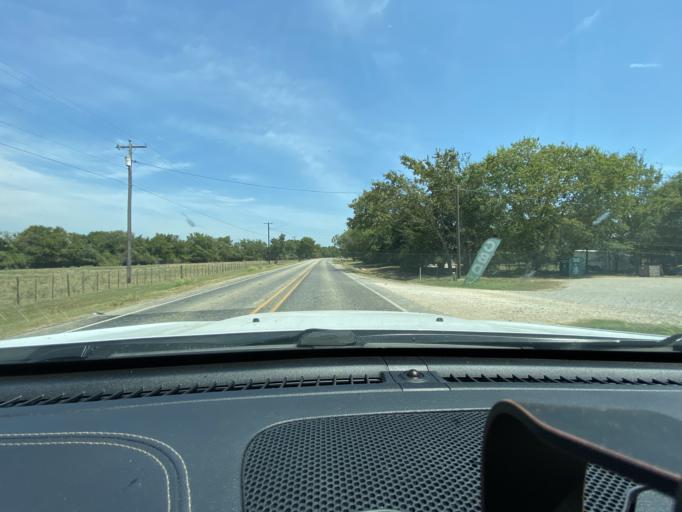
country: US
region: Texas
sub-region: Lee County
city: Giddings
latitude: 30.1707
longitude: -96.9402
